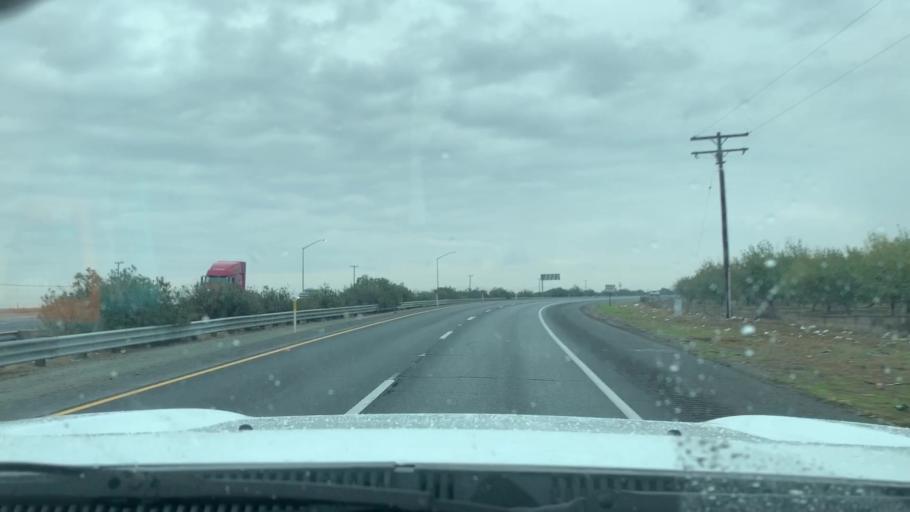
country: US
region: California
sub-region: Kern County
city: Delano
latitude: 35.7926
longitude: -119.2523
